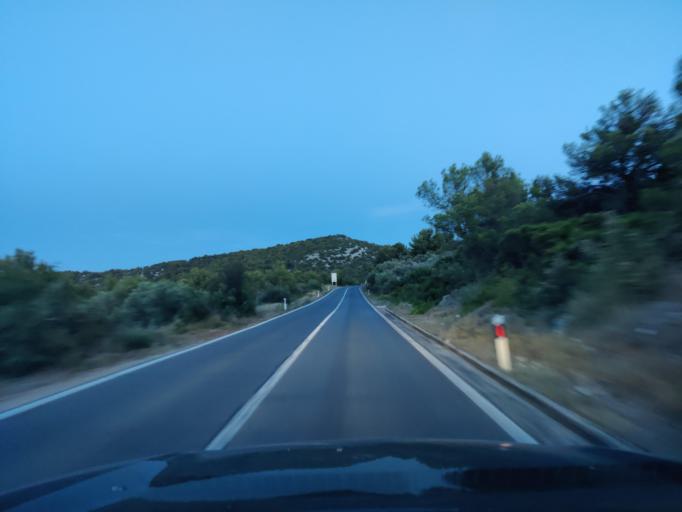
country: HR
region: Sibensko-Kniniska
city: Murter
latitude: 43.8059
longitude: 15.6083
